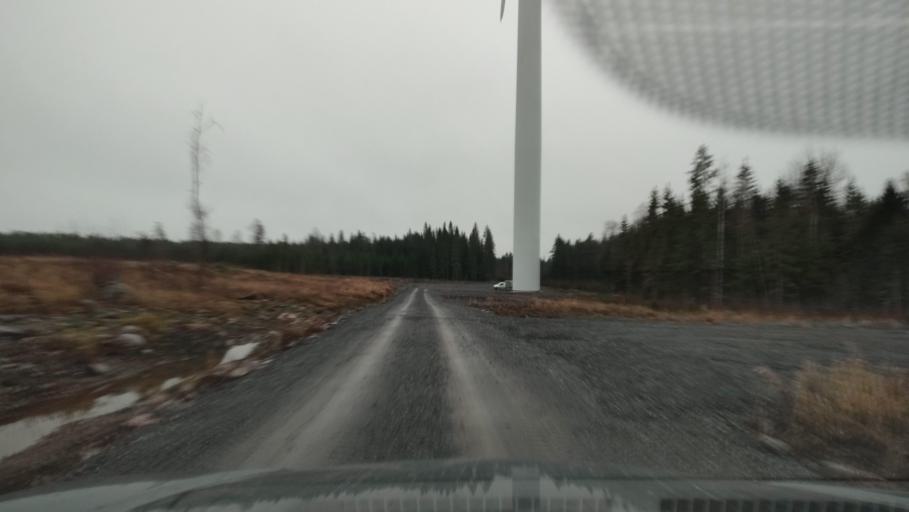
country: FI
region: Southern Ostrobothnia
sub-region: Suupohja
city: Karijoki
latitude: 62.1784
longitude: 21.6025
